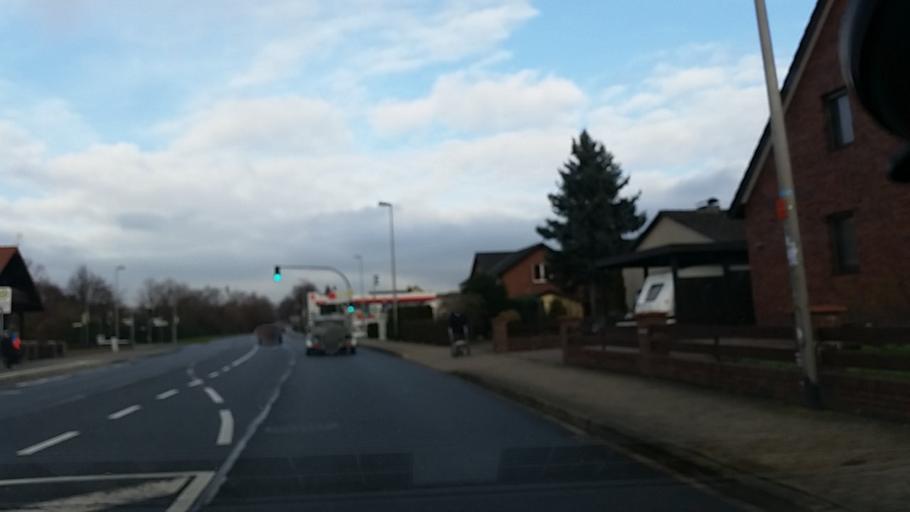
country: DE
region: Lower Saxony
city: Wolfsburg
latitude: 52.4448
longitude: 10.8355
